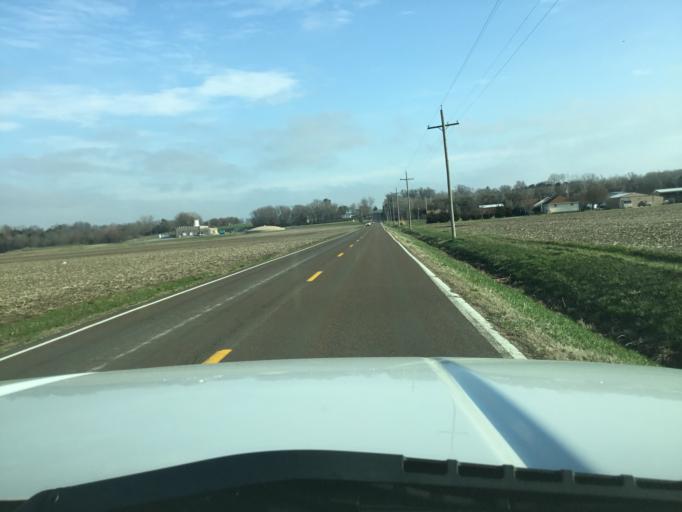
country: US
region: Kansas
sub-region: Shawnee County
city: Topeka
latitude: 39.0997
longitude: -95.7484
